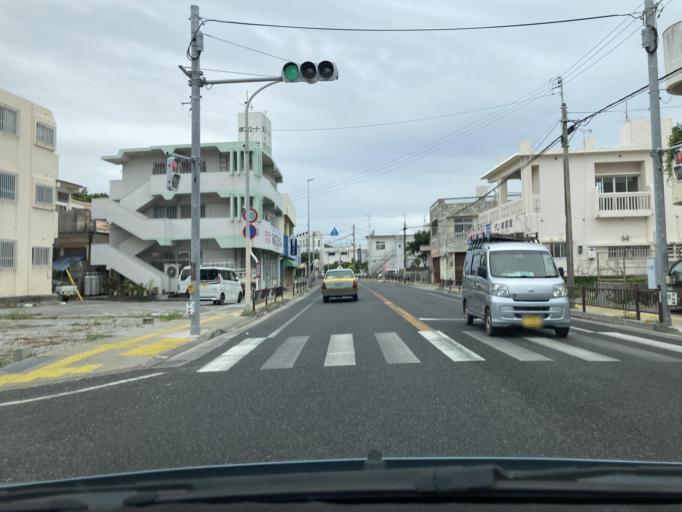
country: JP
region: Okinawa
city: Itoman
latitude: 26.1348
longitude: 127.6697
